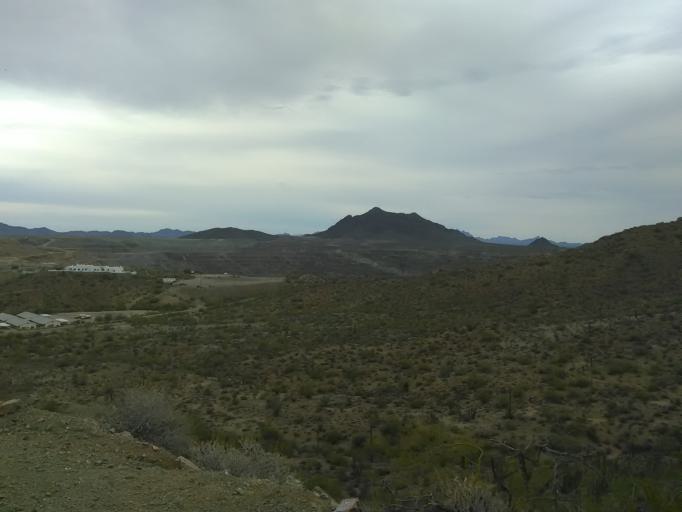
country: US
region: Arizona
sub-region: Pima County
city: Ajo
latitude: 32.3700
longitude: -112.8756
